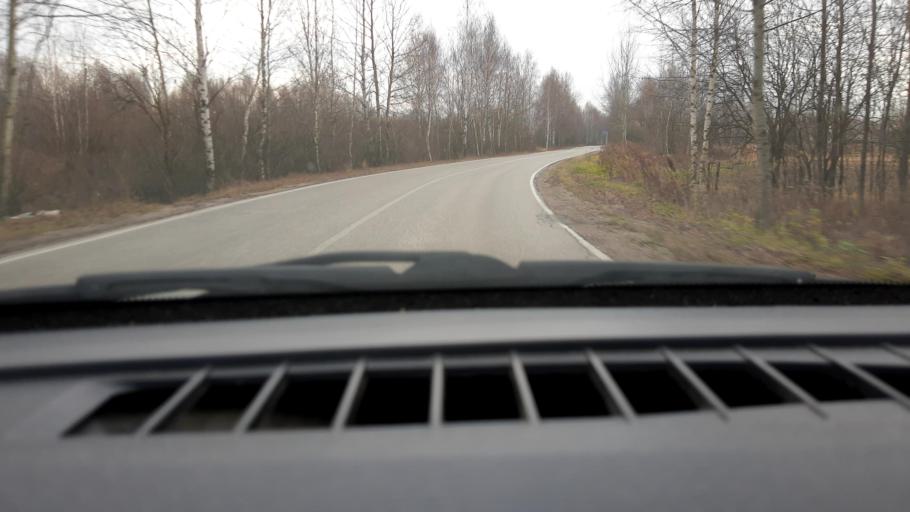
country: RU
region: Nizjnij Novgorod
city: Neklyudovo
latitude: 56.4691
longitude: 43.8907
